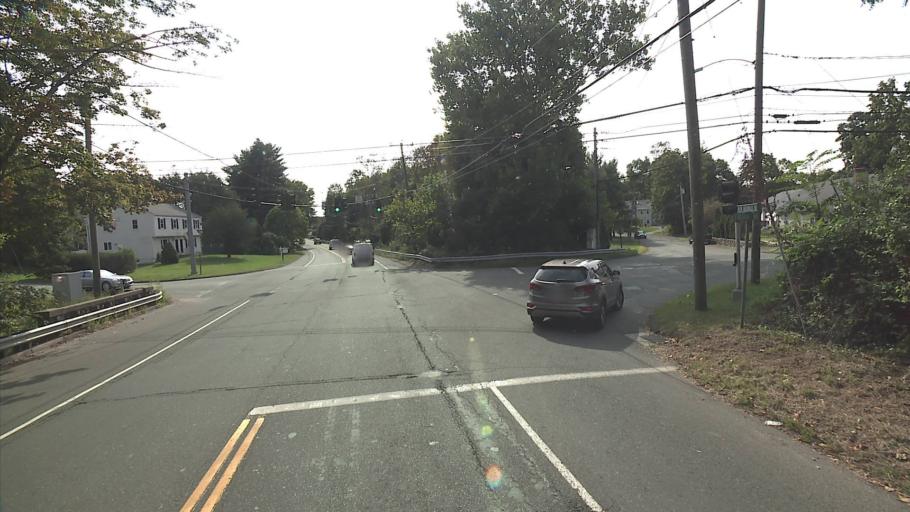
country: US
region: Connecticut
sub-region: Fairfield County
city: New Canaan
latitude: 41.1514
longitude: -73.4898
